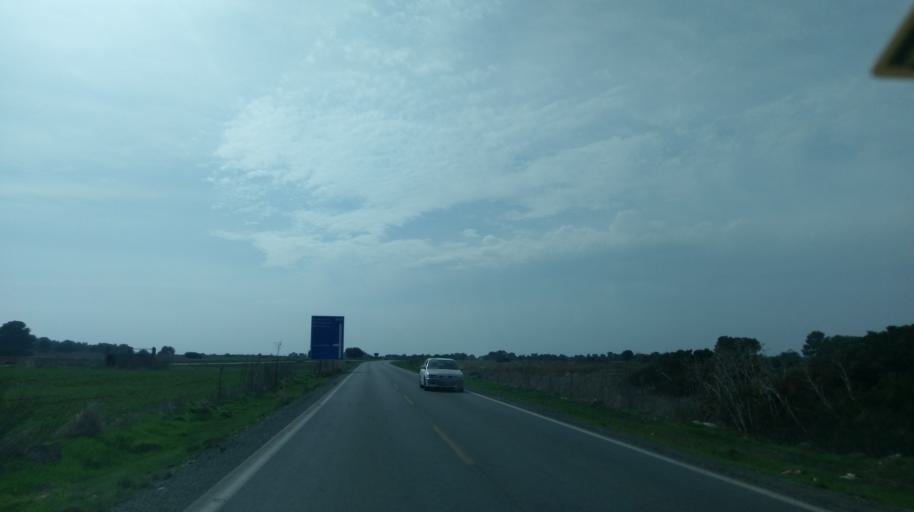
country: CY
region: Lefkosia
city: Morfou
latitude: 35.2990
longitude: 33.0452
